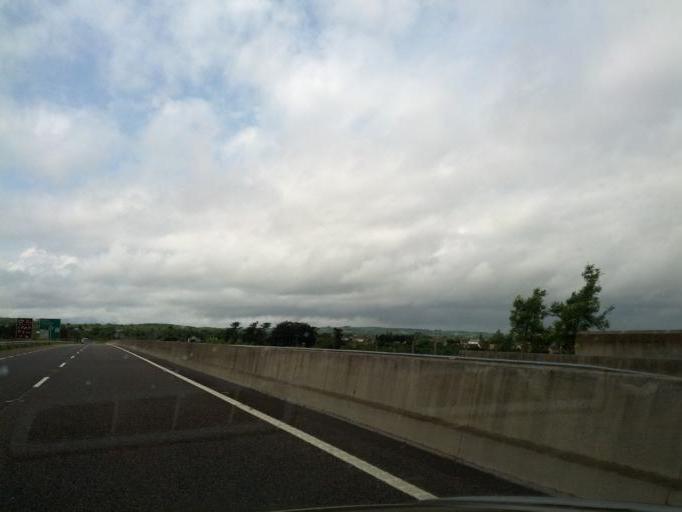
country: IE
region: Munster
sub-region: An Clar
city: Ennis
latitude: 52.8257
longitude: -8.9681
